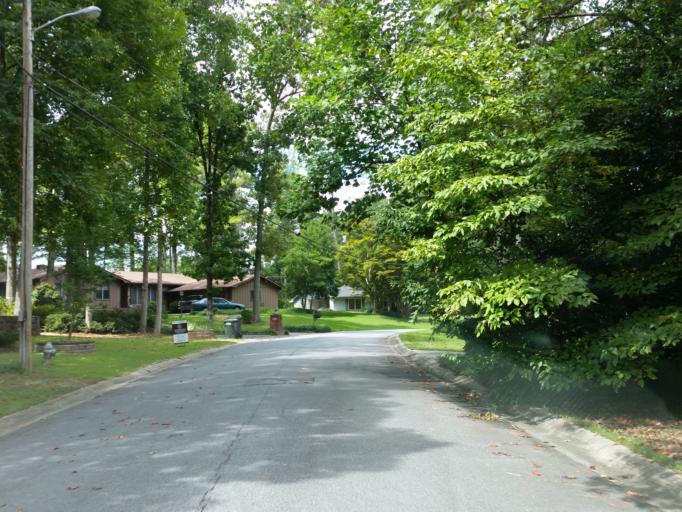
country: US
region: Georgia
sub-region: Cobb County
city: Smyrna
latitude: 33.9473
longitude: -84.4735
